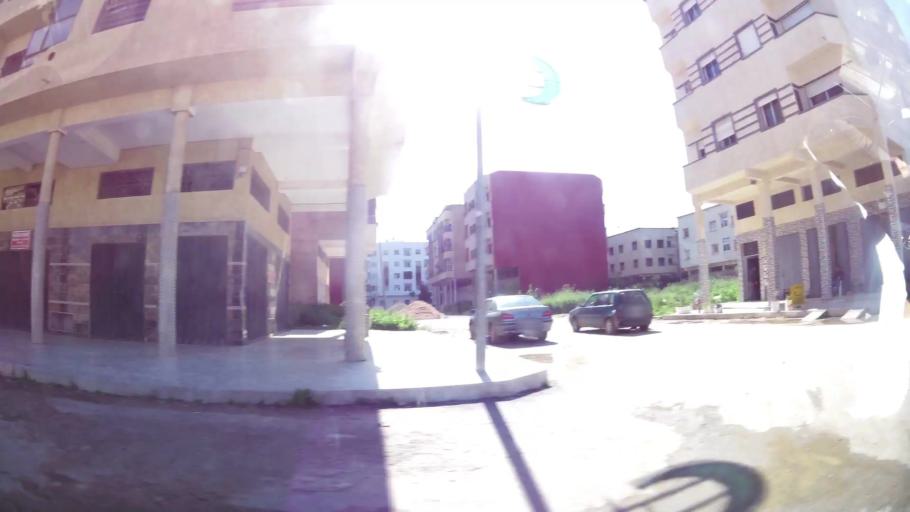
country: MA
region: Grand Casablanca
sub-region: Mediouna
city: Mediouna
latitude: 33.4569
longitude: -7.5082
